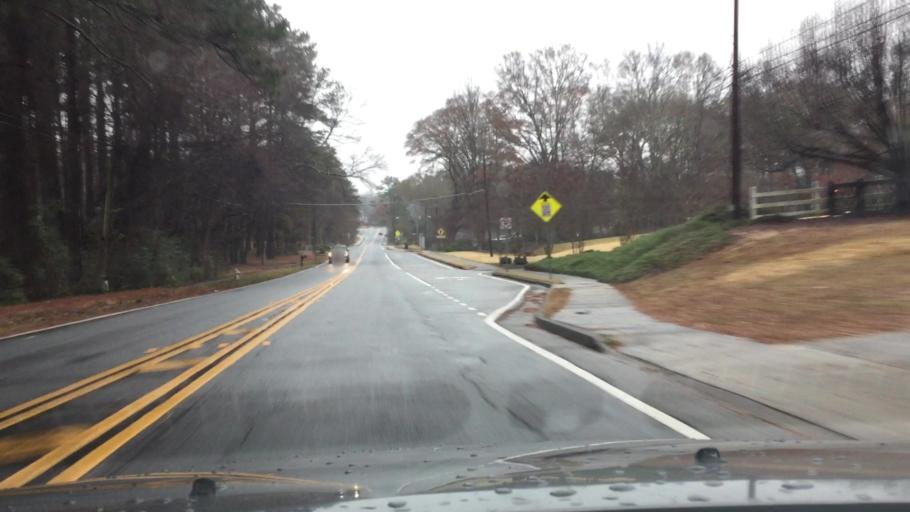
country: US
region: Georgia
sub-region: Cobb County
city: Powder Springs
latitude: 33.8904
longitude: -84.6763
